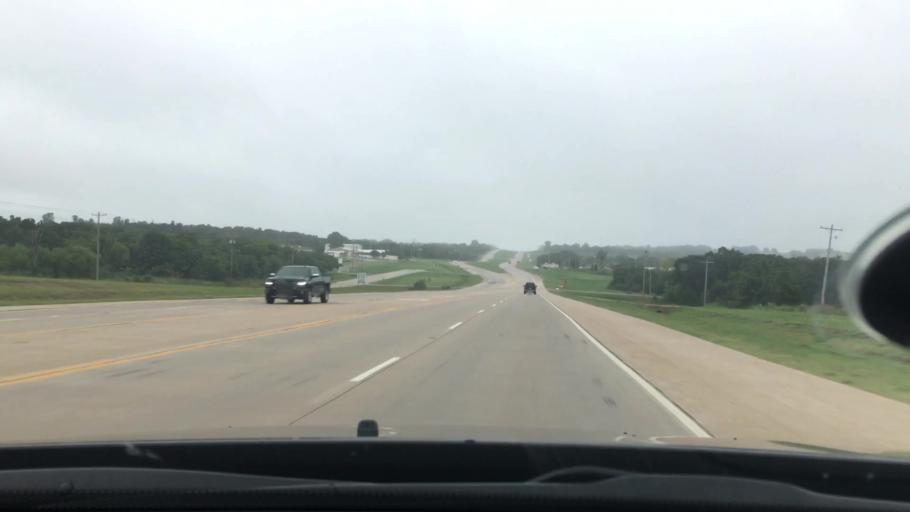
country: US
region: Oklahoma
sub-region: Seminole County
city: Seminole
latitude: 35.2729
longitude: -96.6704
